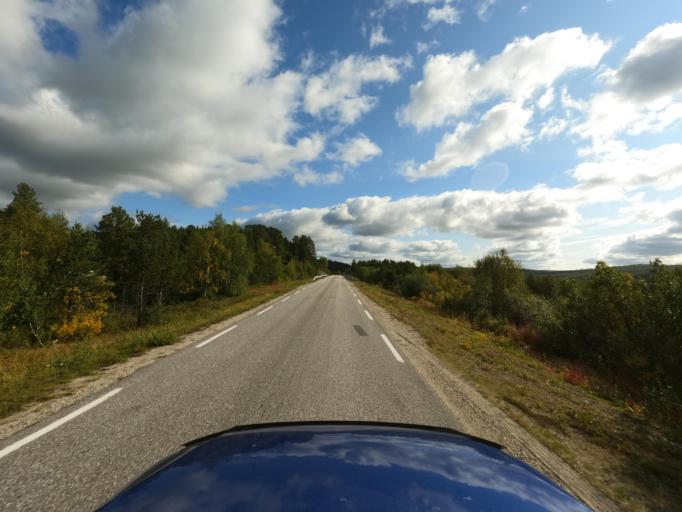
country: NO
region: Finnmark Fylke
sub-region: Karasjok
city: Karasjohka
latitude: 69.4437
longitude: 25.2262
